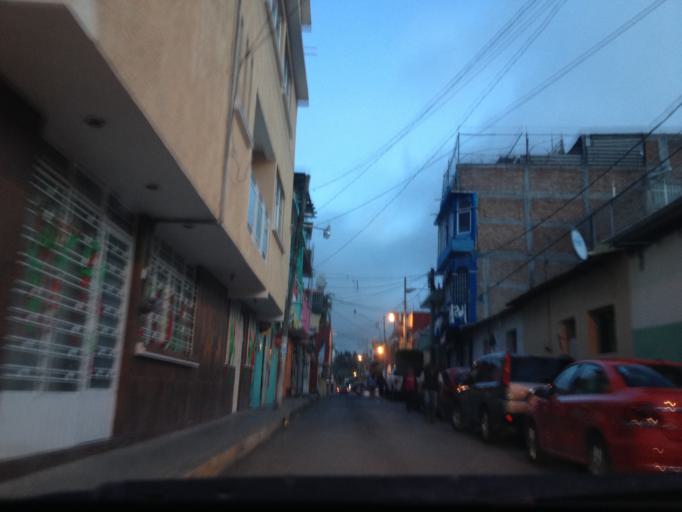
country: MX
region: Guerrero
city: Chilpancingo de los Bravos
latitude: 17.5569
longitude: -99.4995
